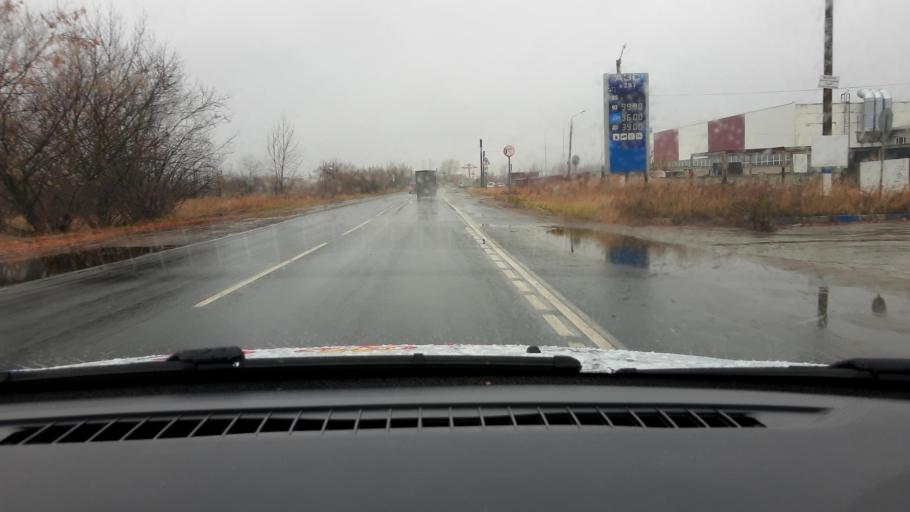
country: RU
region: Nizjnij Novgorod
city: Babino
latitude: 56.2556
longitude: 43.5988
